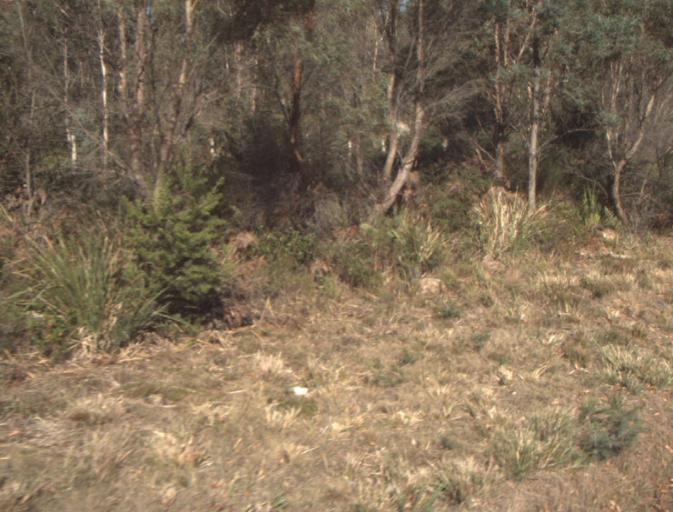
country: AU
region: Tasmania
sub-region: Launceston
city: Mayfield
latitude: -41.3025
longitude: 147.1334
